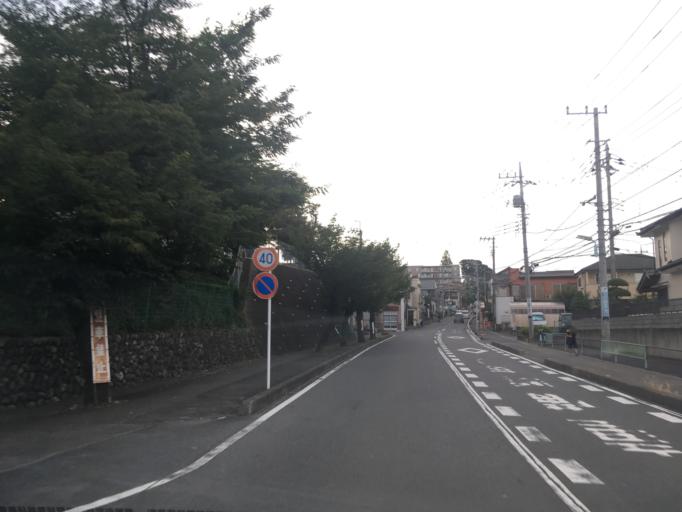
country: JP
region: Saitama
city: Tokorozawa
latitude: 35.7824
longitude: 139.4404
